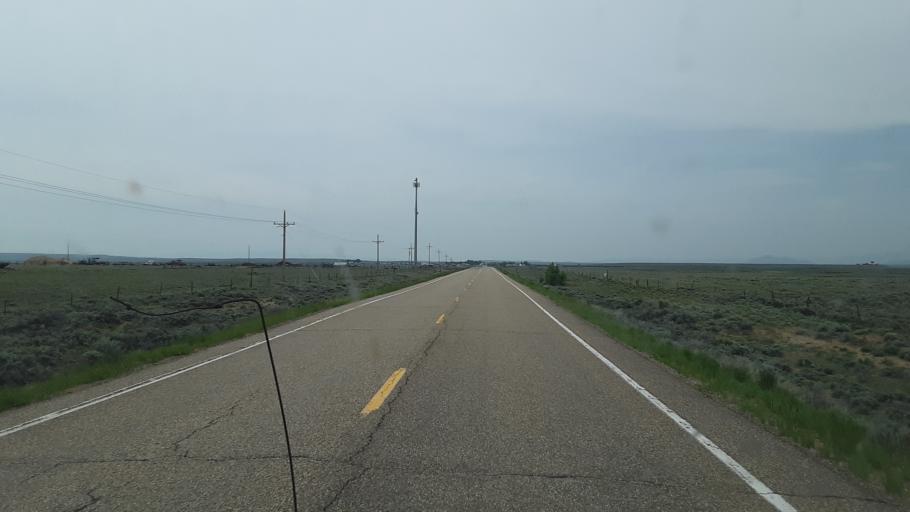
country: US
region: Colorado
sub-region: Jackson County
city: Walden
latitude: 40.8757
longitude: -106.3066
